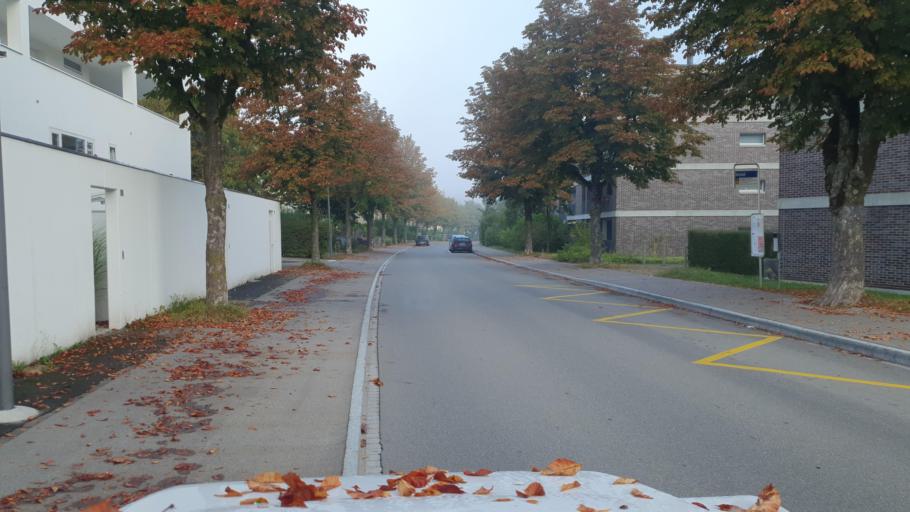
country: CH
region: Aargau
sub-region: Bezirk Baden
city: Baden
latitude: 47.4520
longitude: 8.2840
